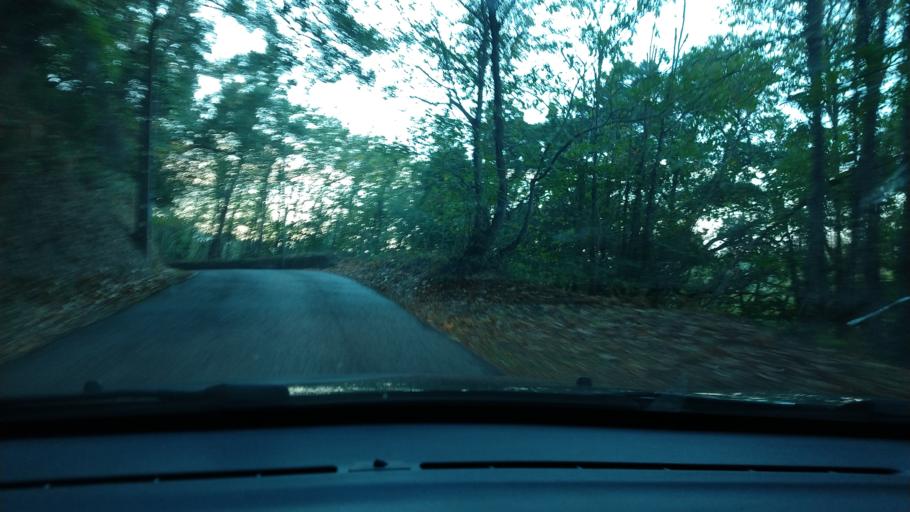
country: PT
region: Lisbon
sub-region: Sintra
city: Colares
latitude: 38.7978
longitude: -9.4393
